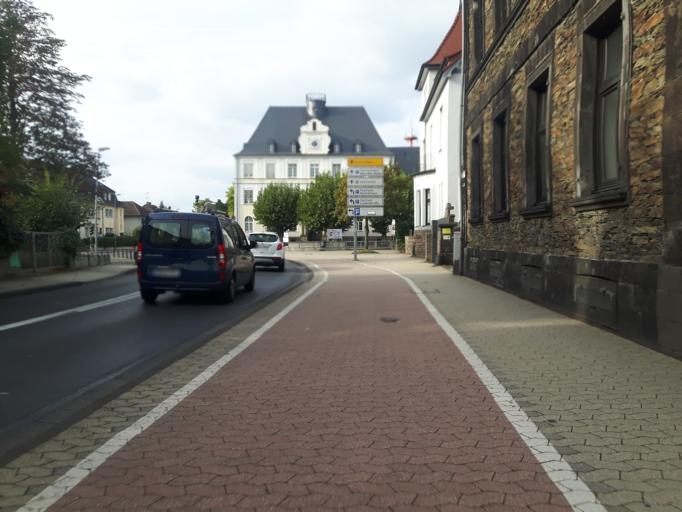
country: DE
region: Rheinland-Pfalz
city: Neuwied
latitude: 50.4312
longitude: 7.4616
